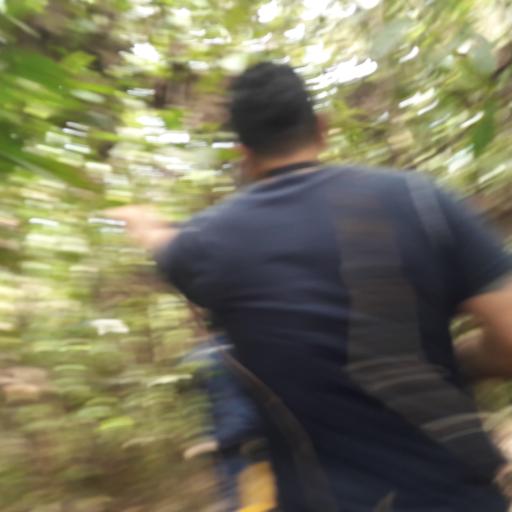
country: EC
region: Napo
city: Tena
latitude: -0.9498
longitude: -77.8618
